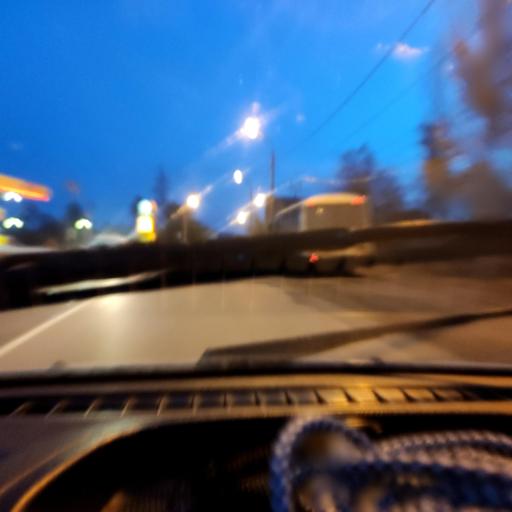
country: RU
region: Samara
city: Zhigulevsk
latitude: 53.4680
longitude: 49.5479
